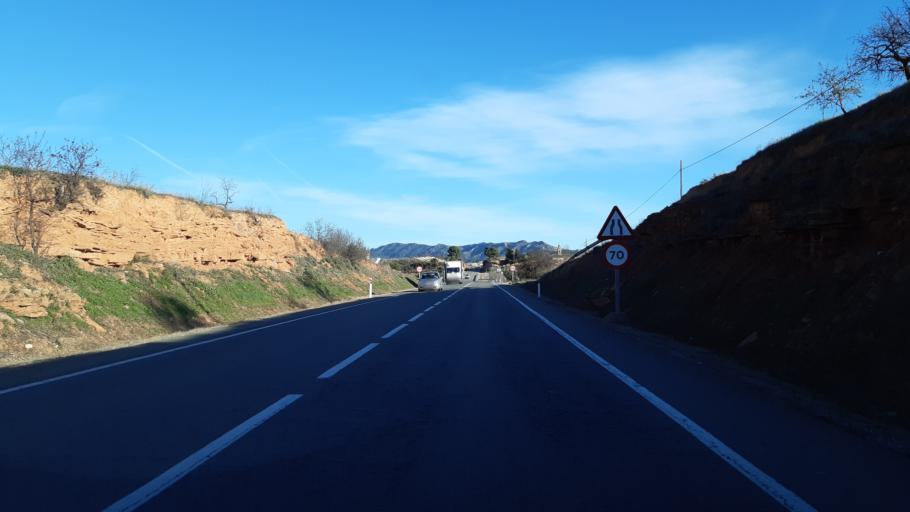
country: ES
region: Catalonia
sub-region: Provincia de Tarragona
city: Gandesa
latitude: 41.0542
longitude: 0.4233
